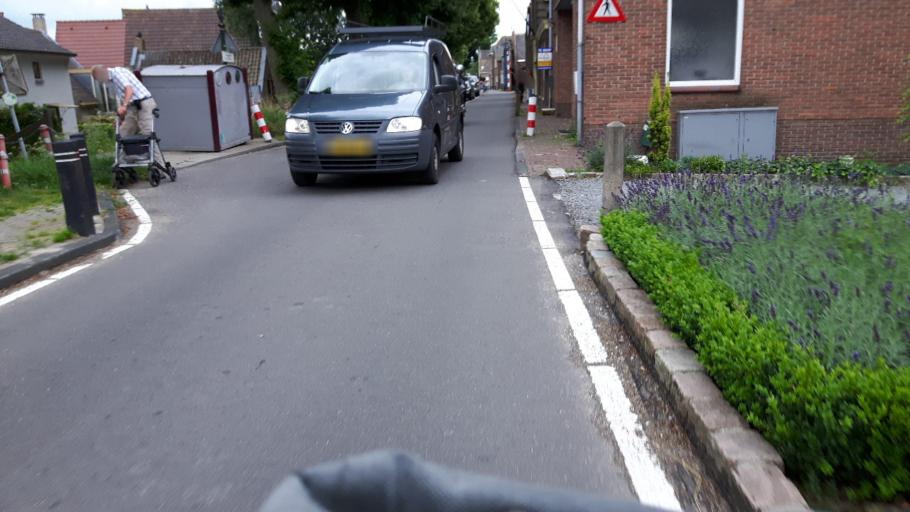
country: NL
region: South Holland
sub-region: Gemeente Vlist
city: Haastrecht
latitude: 52.0145
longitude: 4.8085
